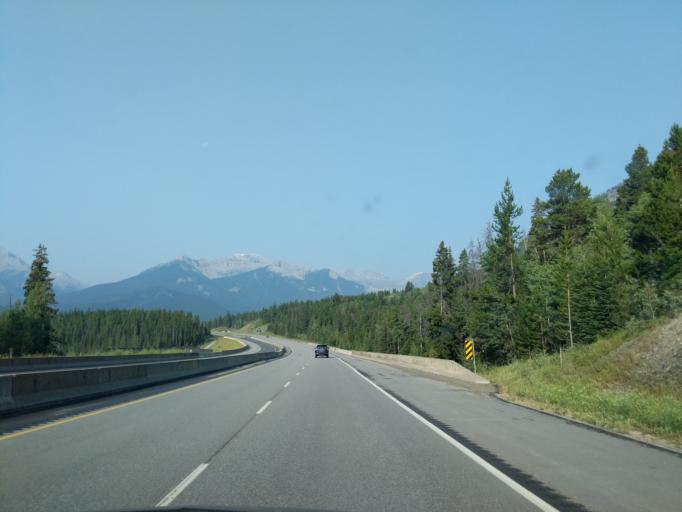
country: CA
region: Alberta
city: Banff
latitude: 51.1759
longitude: -115.6424
